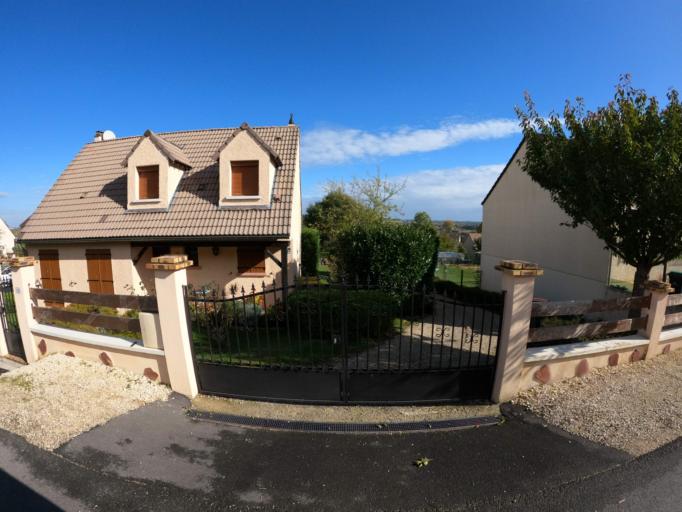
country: FR
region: Ile-de-France
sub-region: Departement de Seine-et-Marne
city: Montry
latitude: 48.8850
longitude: 2.8249
